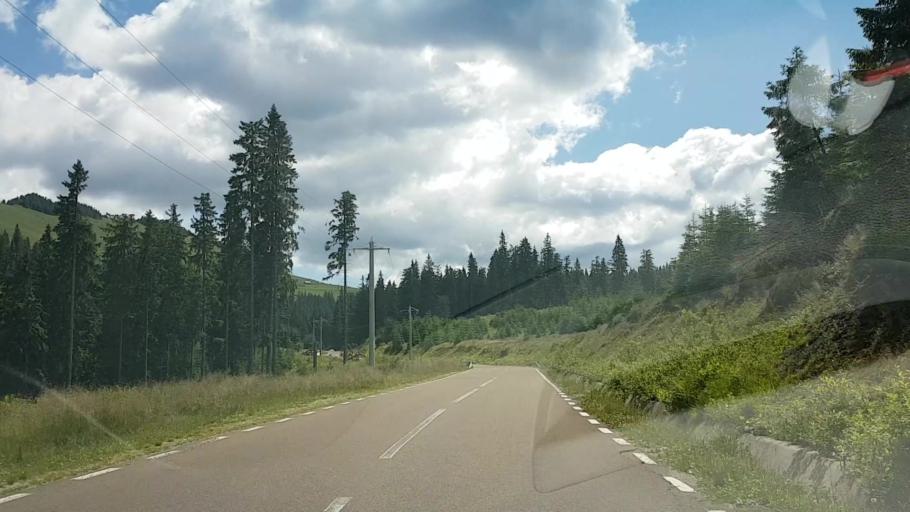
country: RO
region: Suceava
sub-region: Comuna Sadova
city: Sadova
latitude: 47.4587
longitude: 25.5173
